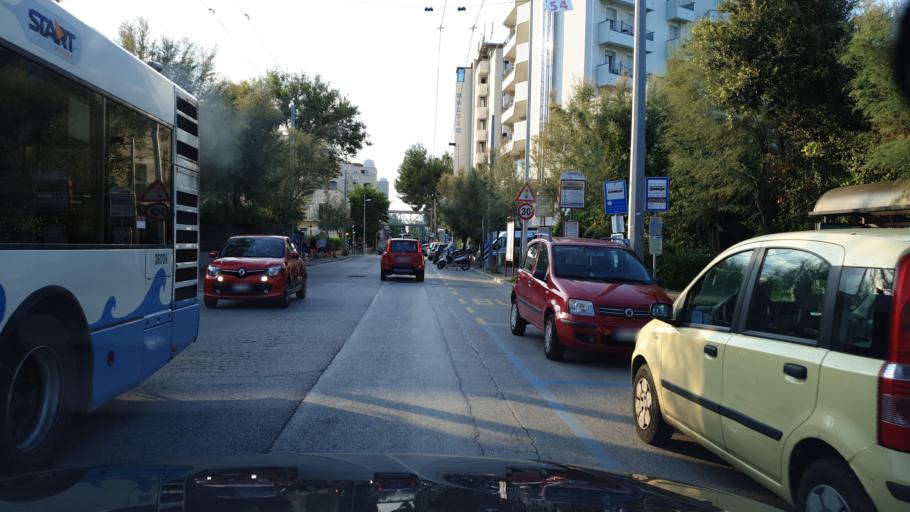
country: IT
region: Emilia-Romagna
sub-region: Provincia di Rimini
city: Riccione
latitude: 43.9960
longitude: 12.6712
